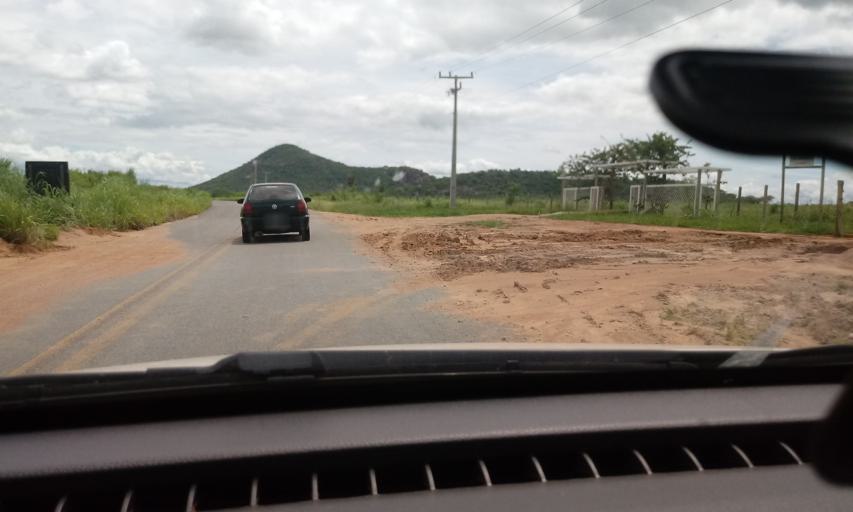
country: BR
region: Bahia
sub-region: Guanambi
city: Guanambi
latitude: -14.1467
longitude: -42.8335
